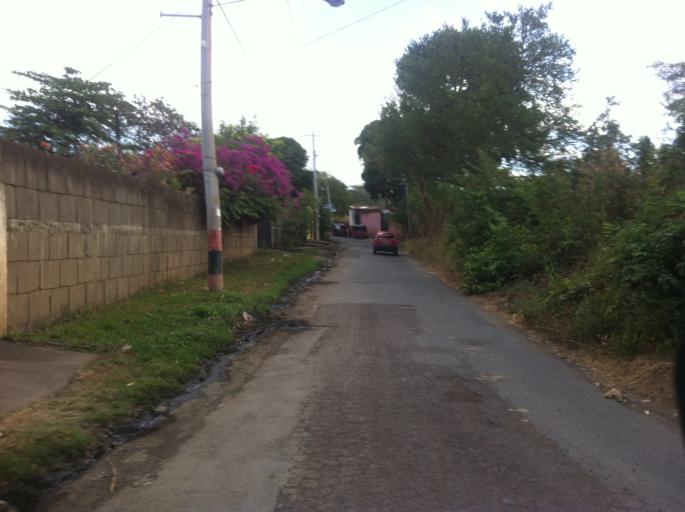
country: NI
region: Managua
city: Ciudad Sandino
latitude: 12.1085
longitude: -86.3141
